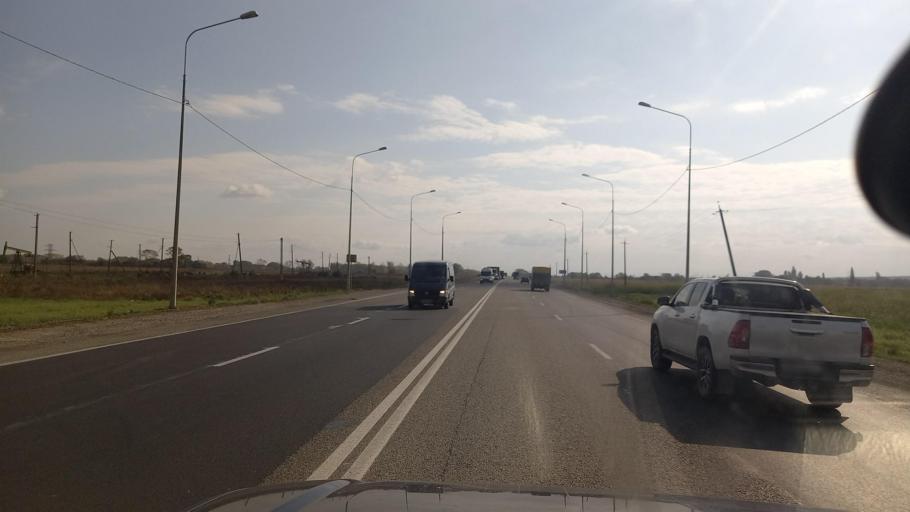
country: RU
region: Krasnodarskiy
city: Novoukrainskiy
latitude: 44.8934
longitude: 38.0645
